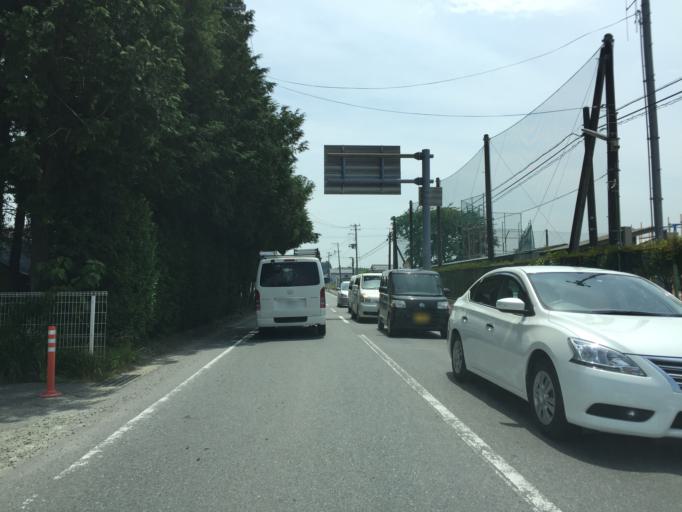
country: JP
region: Fukushima
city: Namie
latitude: 37.6345
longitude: 140.9352
